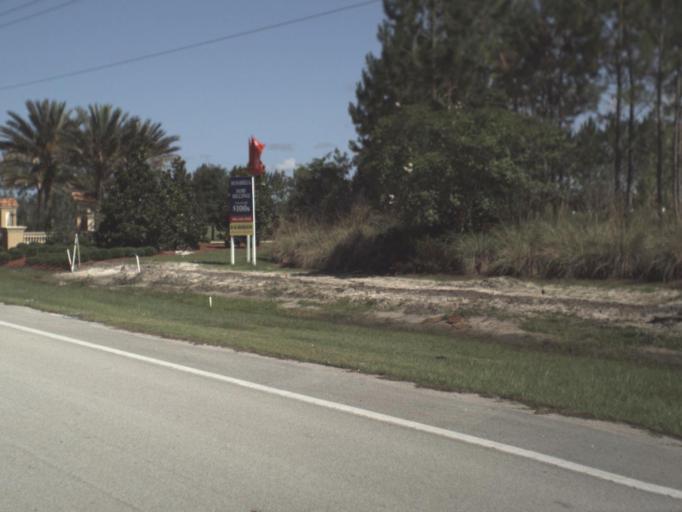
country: US
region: Florida
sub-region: Saint Johns County
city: Saint Augustine
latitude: 29.9621
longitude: -81.4823
